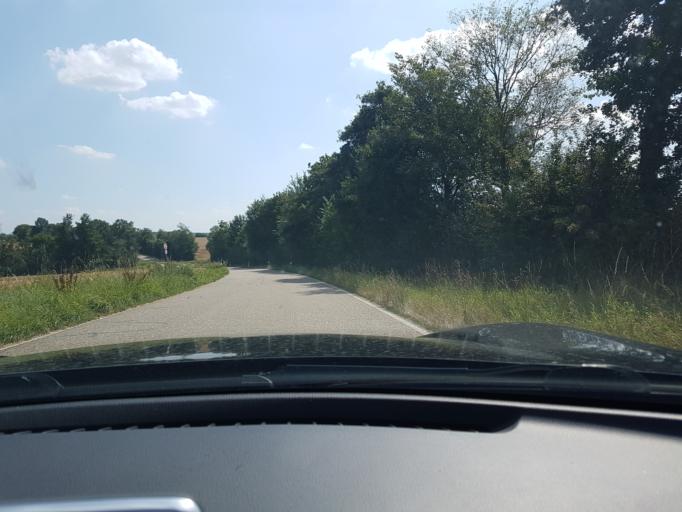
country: DE
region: Baden-Wuerttemberg
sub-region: Regierungsbezirk Stuttgart
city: Gundelsheim
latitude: 49.2703
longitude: 9.1349
